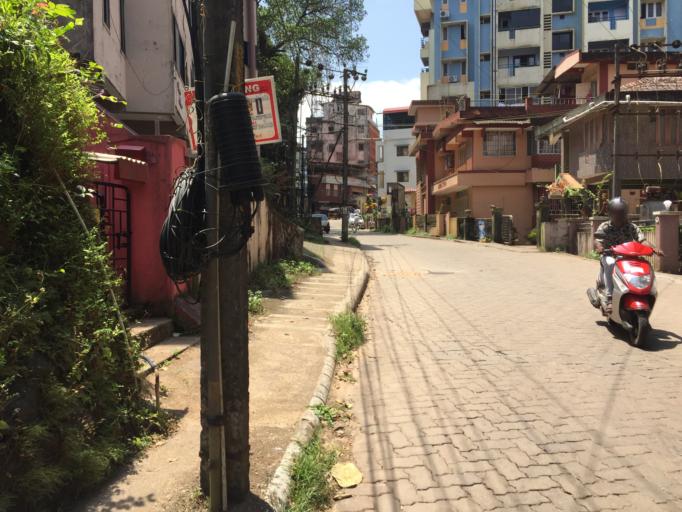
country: IN
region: Karnataka
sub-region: Dakshina Kannada
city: Mangalore
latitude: 12.8747
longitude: 74.8519
